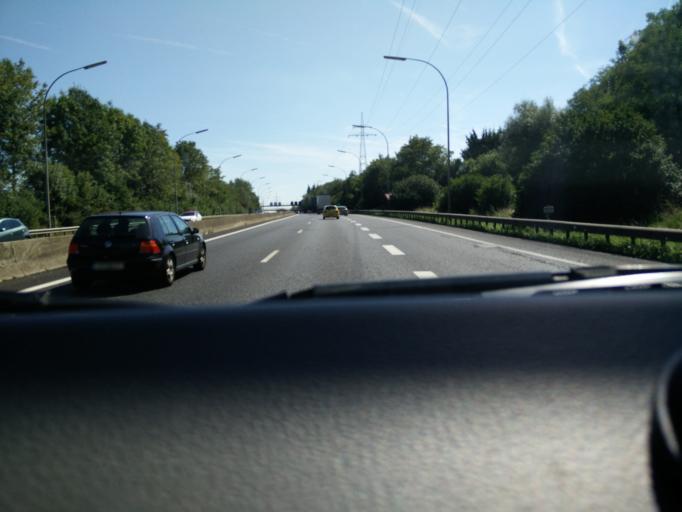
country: LU
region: Luxembourg
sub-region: Canton d'Esch-sur-Alzette
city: Leudelange
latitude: 49.5829
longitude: 6.0918
